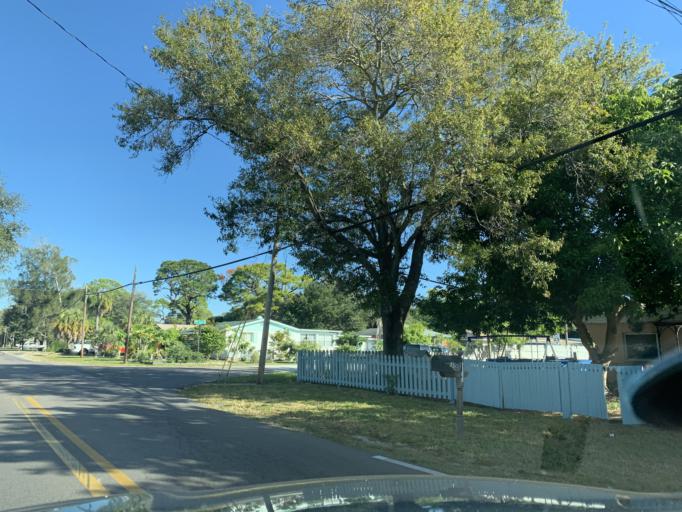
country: US
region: Florida
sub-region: Pinellas County
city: Kenneth City
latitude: 27.8162
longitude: -82.7368
